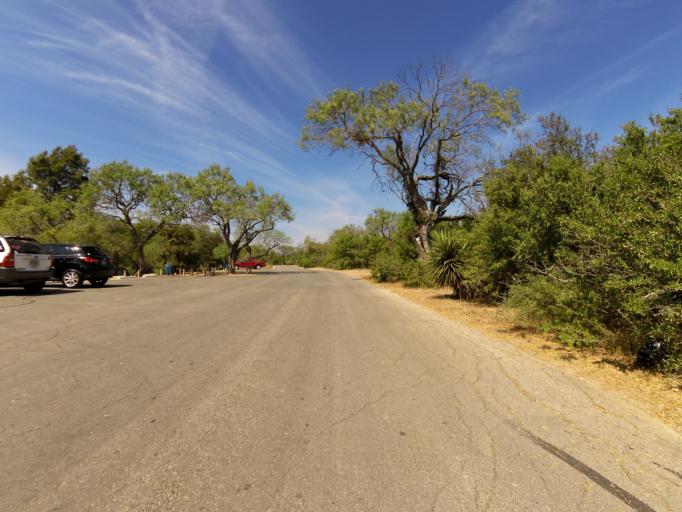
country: US
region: Texas
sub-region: Bexar County
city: San Antonio
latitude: 29.3873
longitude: -98.4269
